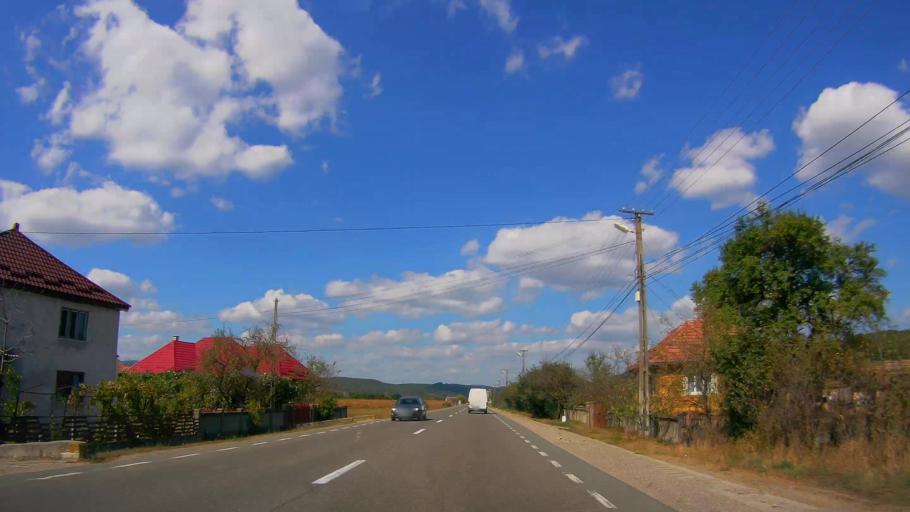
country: RO
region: Salaj
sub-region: Comuna Romanasi
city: Romanasi
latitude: 47.0943
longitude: 23.1889
